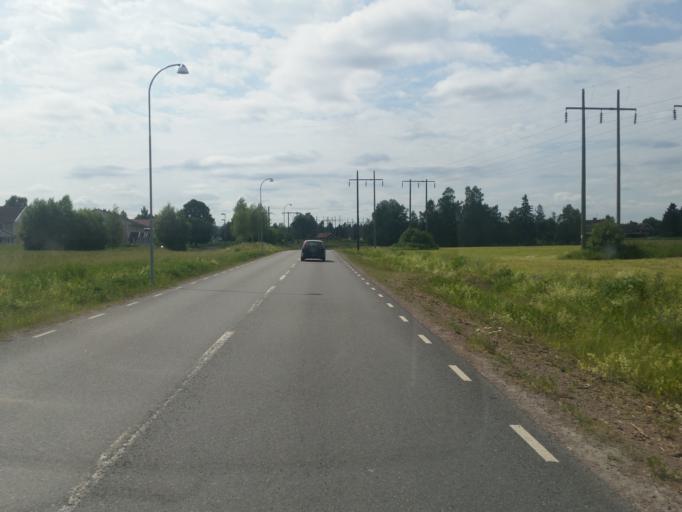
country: SE
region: Dalarna
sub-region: Leksand Municipality
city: Smedby
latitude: 60.6838
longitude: 15.0882
